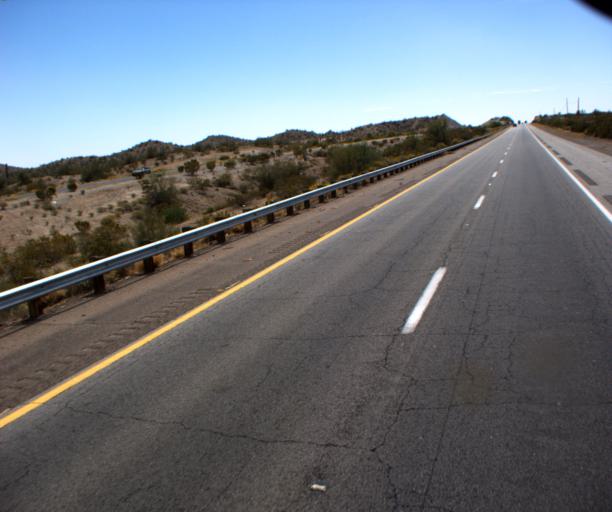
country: US
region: Arizona
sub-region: Maricopa County
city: Buckeye
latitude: 33.3079
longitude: -112.6259
